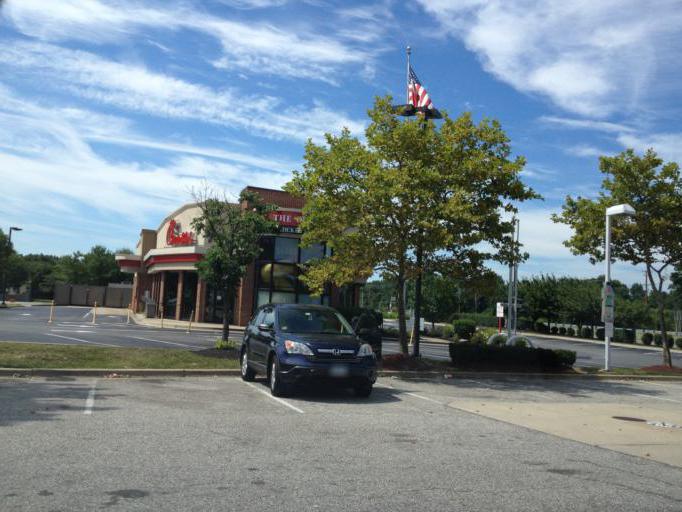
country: US
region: Maryland
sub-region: Prince George's County
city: Bowie
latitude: 38.9449
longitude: -76.7168
